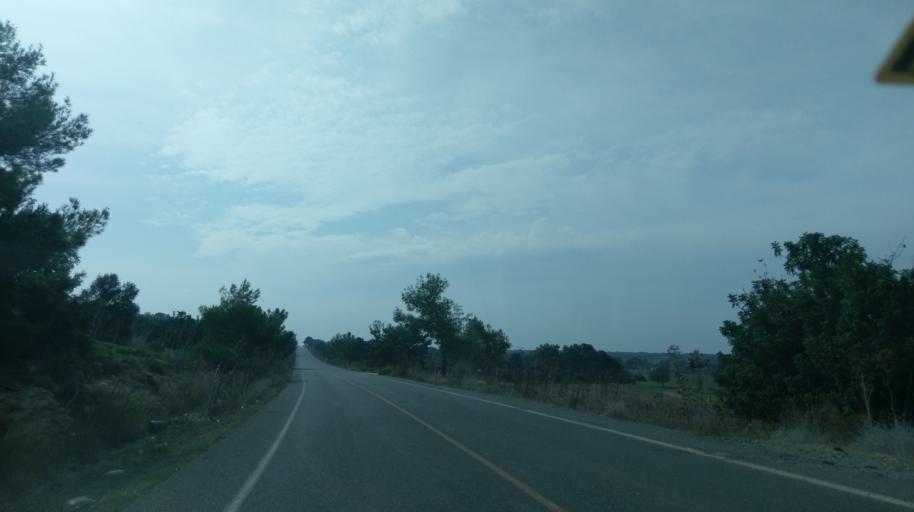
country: CY
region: Lefkosia
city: Morfou
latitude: 35.3115
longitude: 33.0489
